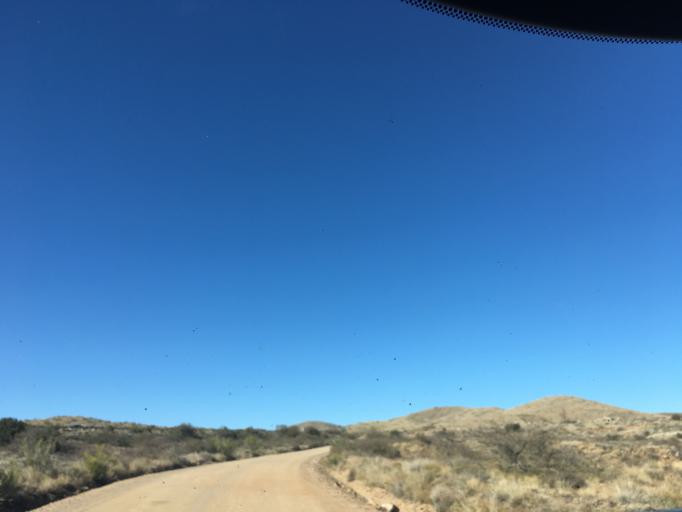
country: US
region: Arizona
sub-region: Yavapai County
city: Cordes Lakes
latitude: 34.2730
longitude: -112.1121
